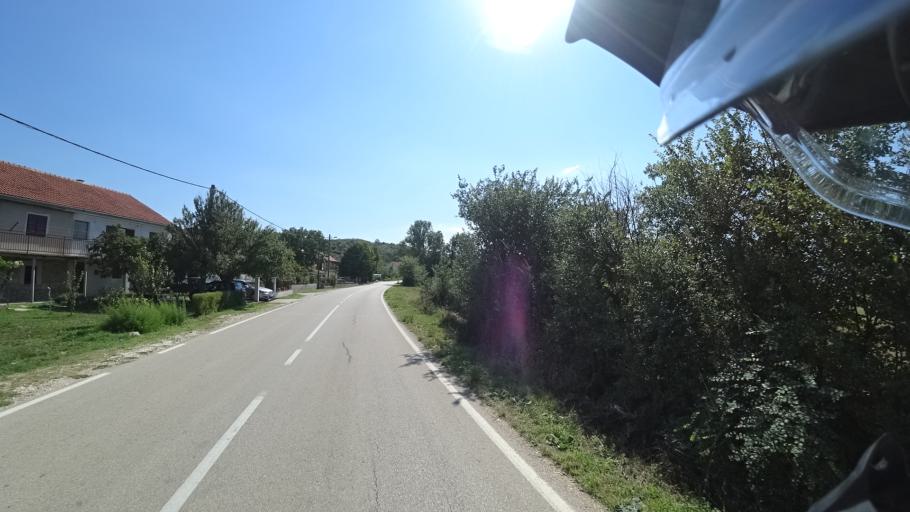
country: HR
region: Sibensko-Kniniska
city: Drnis
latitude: 43.8582
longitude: 16.2270
